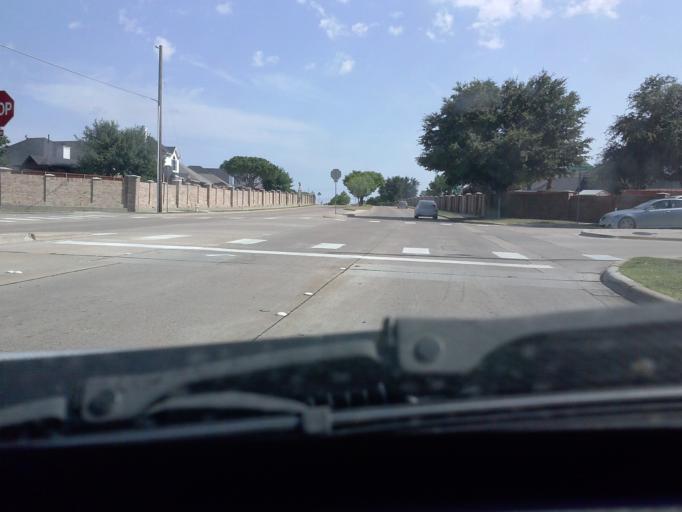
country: US
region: Texas
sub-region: Collin County
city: Frisco
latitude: 33.0655
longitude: -96.7923
